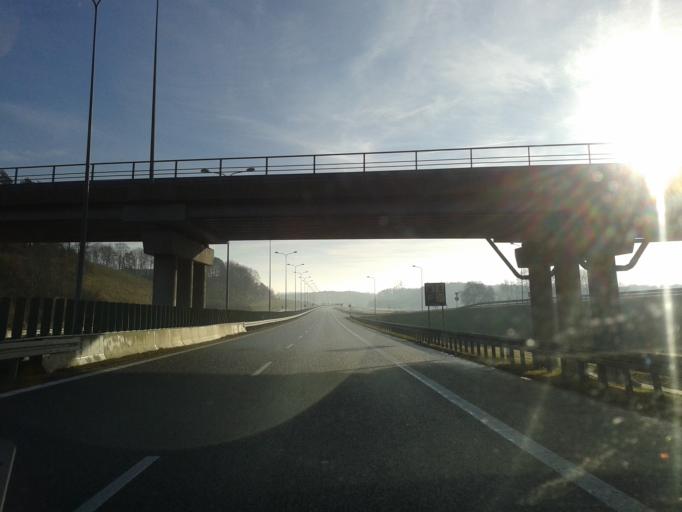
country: PL
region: Greater Poland Voivodeship
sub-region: Powiat pilski
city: Wyrzysk
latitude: 53.1575
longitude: 17.3043
